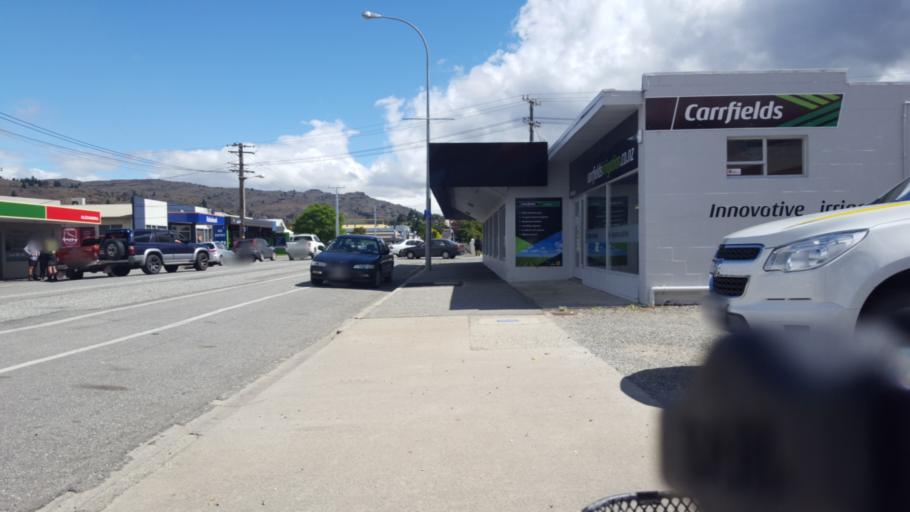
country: NZ
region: Otago
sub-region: Queenstown-Lakes District
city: Wanaka
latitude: -45.2529
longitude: 169.3946
